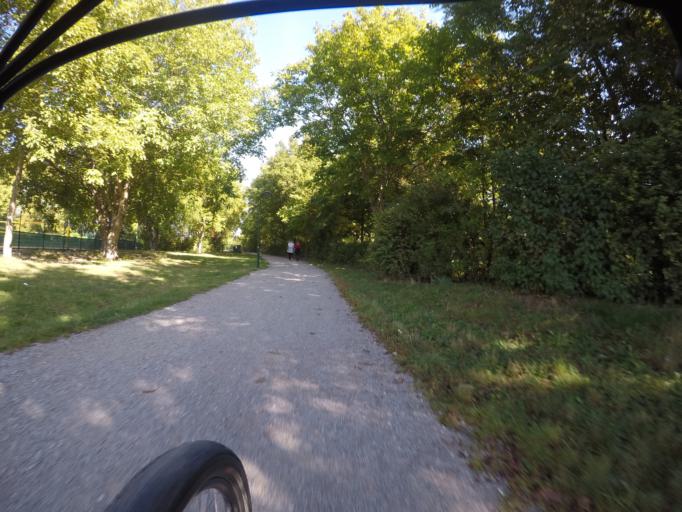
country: AT
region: Lower Austria
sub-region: Politischer Bezirk Modling
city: Brunn am Gebirge
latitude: 48.1039
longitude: 16.2989
